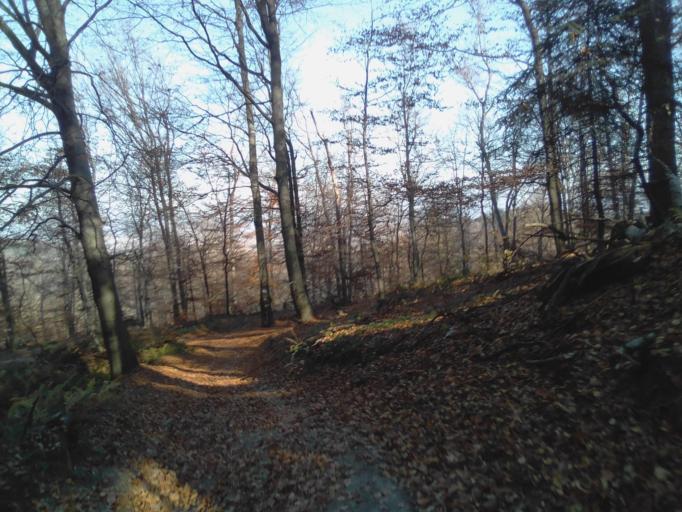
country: PL
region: Subcarpathian Voivodeship
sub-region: Powiat krosnienski
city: Leki
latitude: 49.8213
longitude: 21.6975
